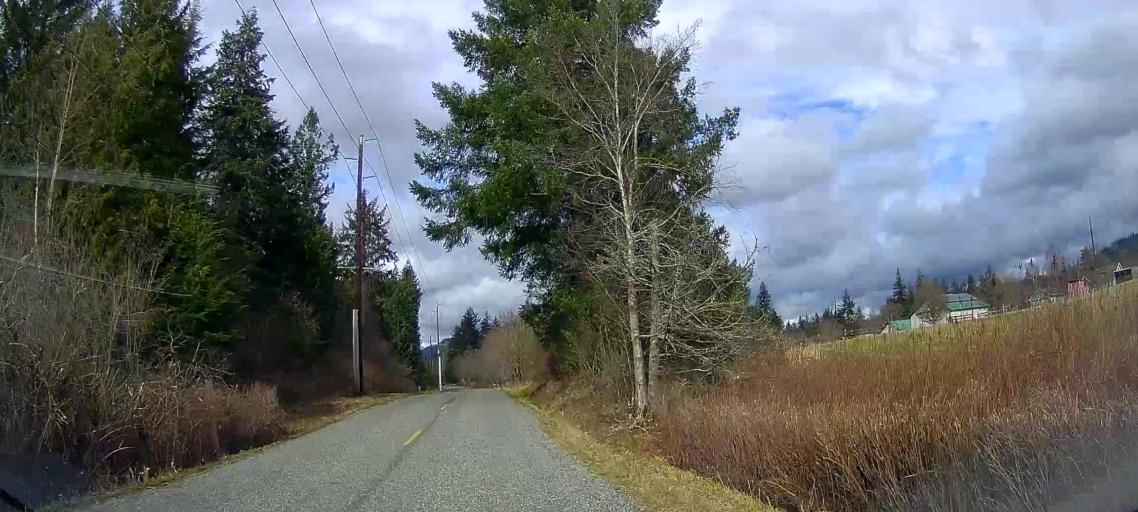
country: US
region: Washington
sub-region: Whatcom County
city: Sudden Valley
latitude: 48.6063
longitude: -122.3332
